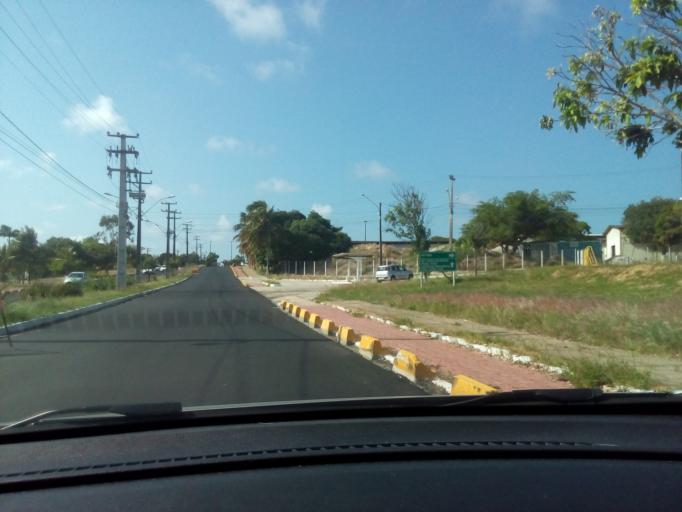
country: BR
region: Rio Grande do Norte
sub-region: Natal
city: Natal
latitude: -5.8398
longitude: -35.2044
